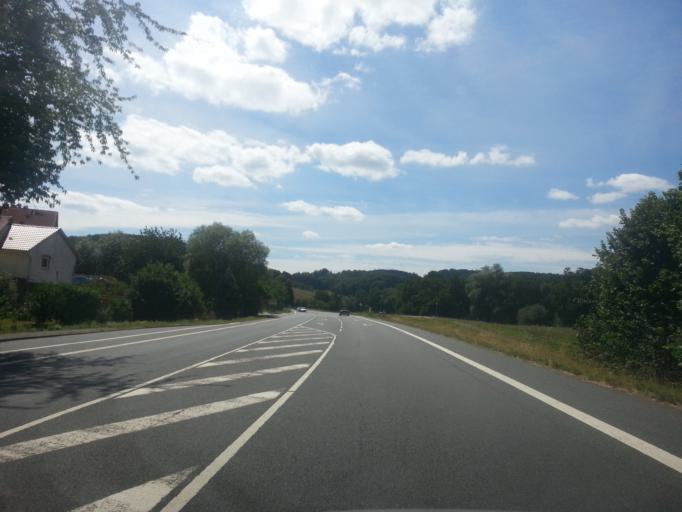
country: DE
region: Hesse
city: Reichelsheim
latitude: 49.7098
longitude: 8.8646
